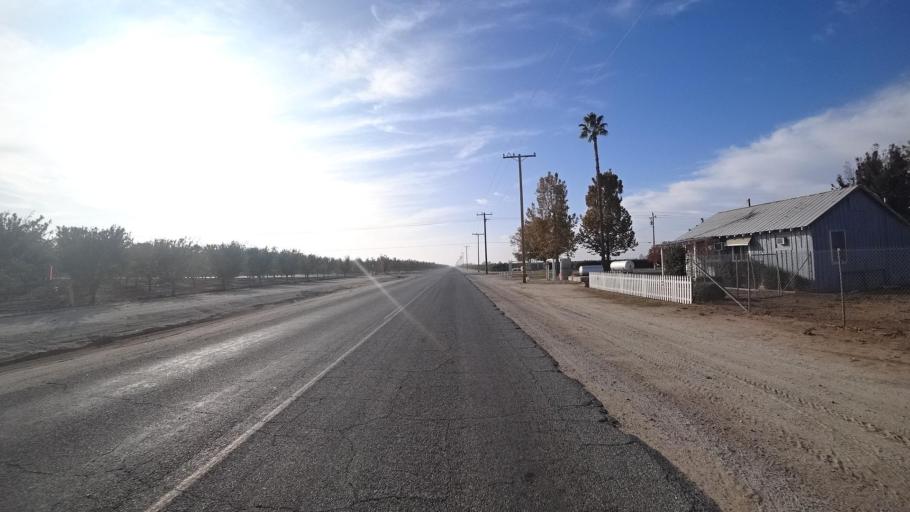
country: US
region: California
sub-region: Kern County
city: McFarland
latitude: 35.6899
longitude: -119.2049
